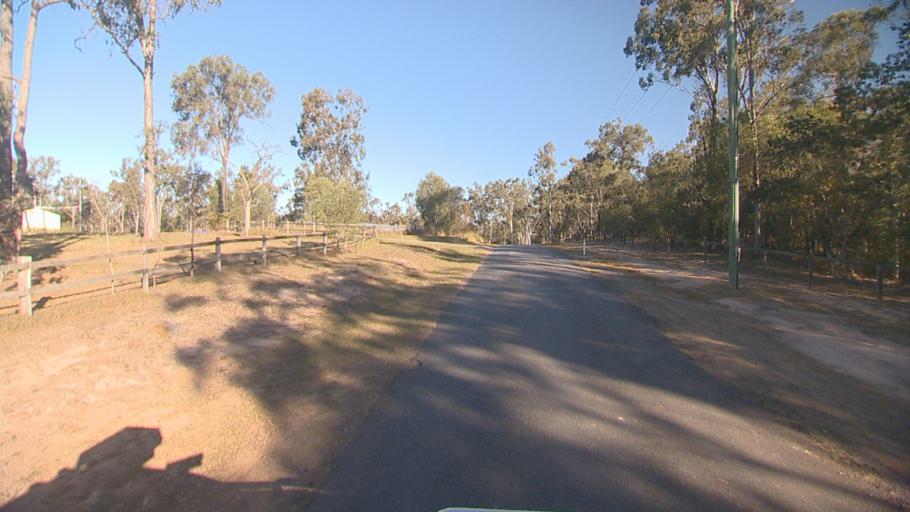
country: AU
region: Queensland
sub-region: Logan
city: North Maclean
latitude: -27.8107
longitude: 153.0409
